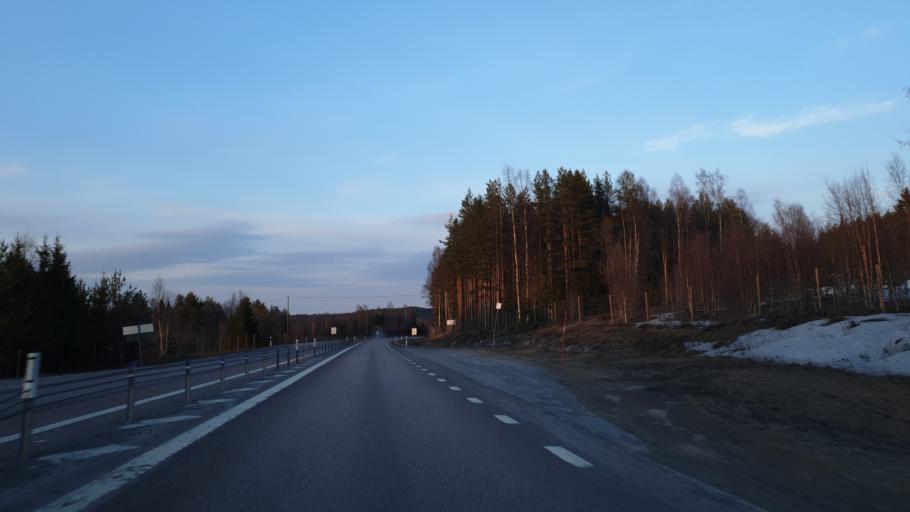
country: SE
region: Vaesternorrland
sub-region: Haernoesands Kommun
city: Haernoesand
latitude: 62.6113
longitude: 17.8407
